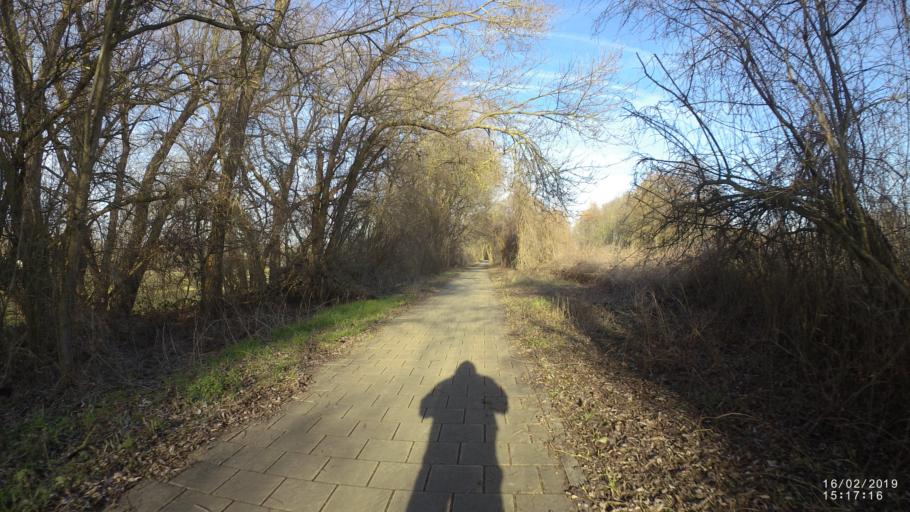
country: BE
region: Flanders
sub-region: Provincie Vlaams-Brabant
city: Hoegaarden
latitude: 50.7784
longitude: 4.9079
